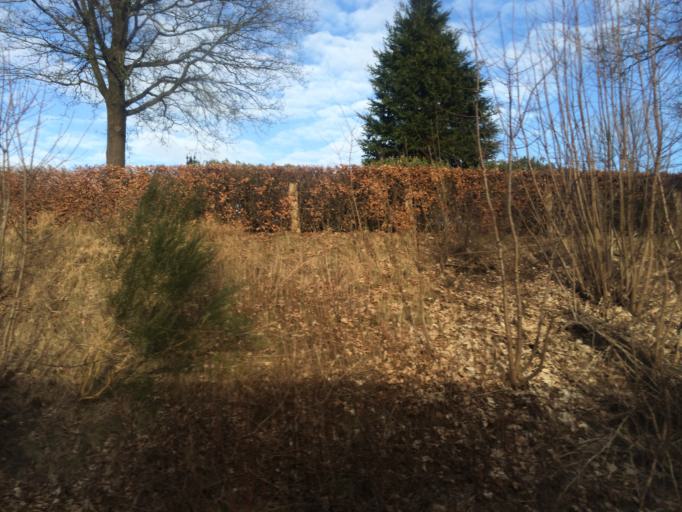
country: DK
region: Central Jutland
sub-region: Herning Kommune
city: Herning
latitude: 56.1337
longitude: 8.9563
